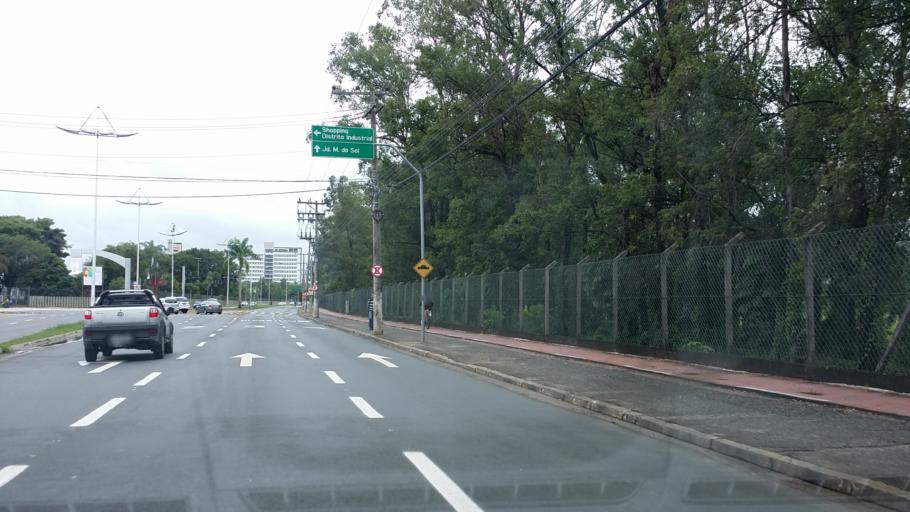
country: BR
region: Sao Paulo
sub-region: Indaiatuba
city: Indaiatuba
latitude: -23.1110
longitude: -47.2200
